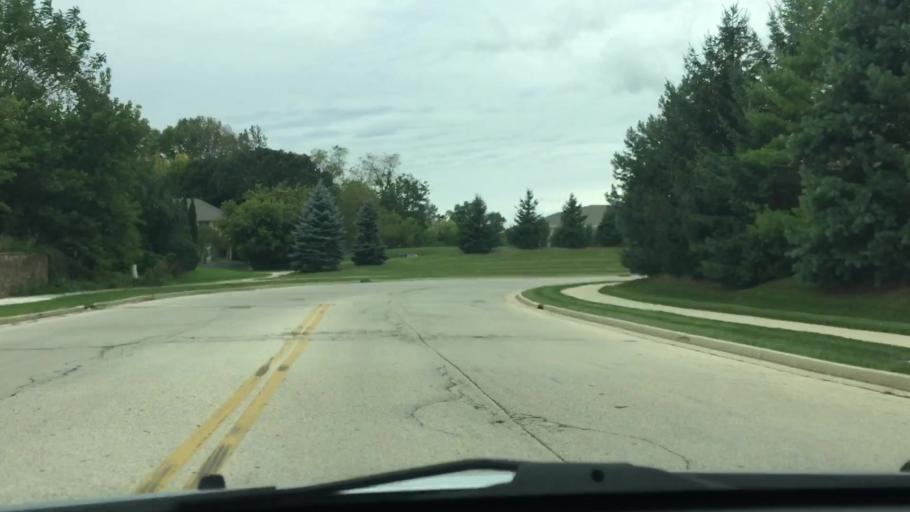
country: US
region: Wisconsin
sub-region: Waukesha County
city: Waukesha
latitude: 43.0396
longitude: -88.2575
